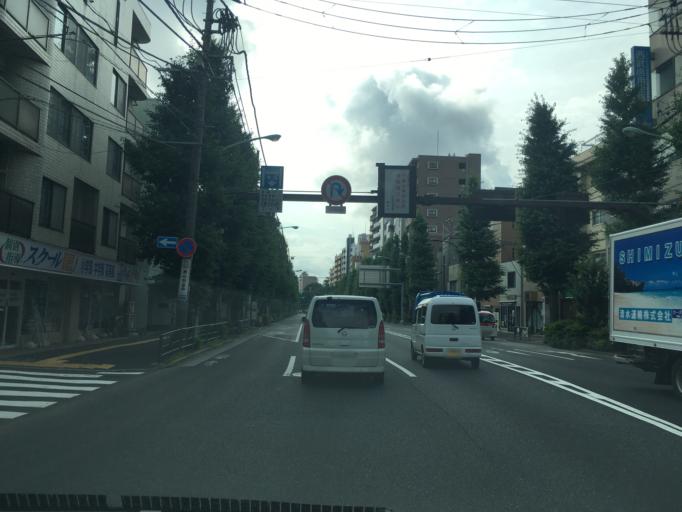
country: JP
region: Tokyo
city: Musashino
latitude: 35.7121
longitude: 139.6023
